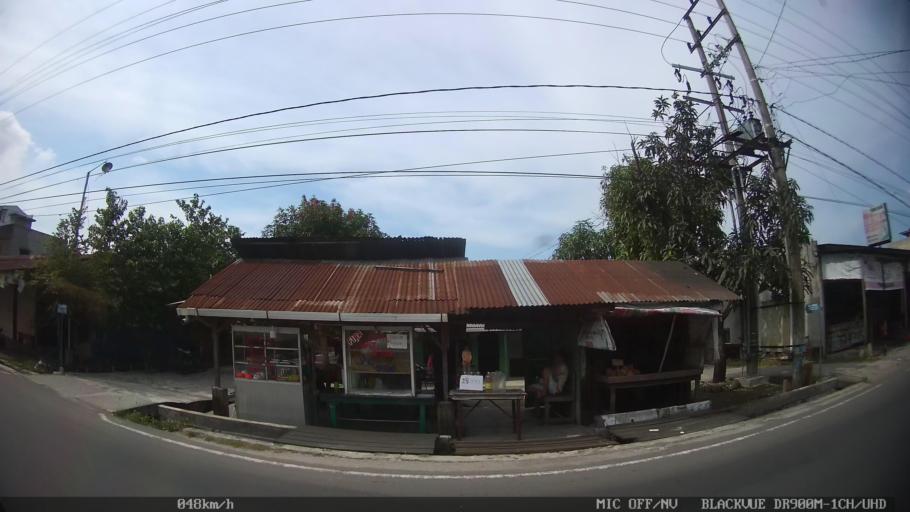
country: ID
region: North Sumatra
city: Percut
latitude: 3.6074
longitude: 98.7775
